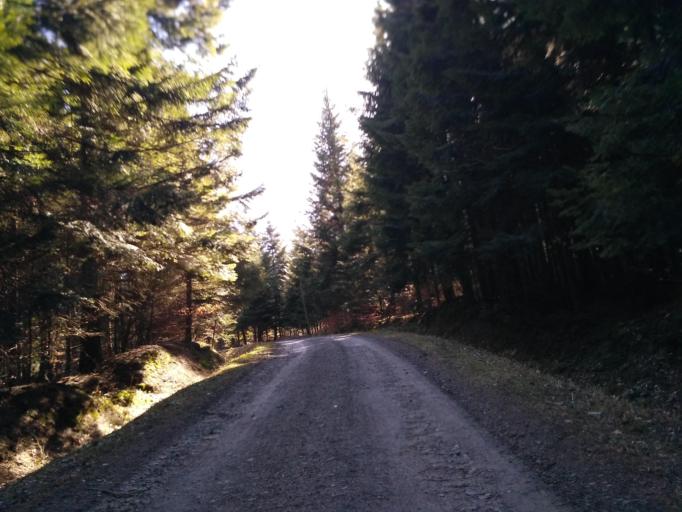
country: PL
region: Subcarpathian Voivodeship
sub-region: Powiat strzyzowski
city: Babica
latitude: 49.9537
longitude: 21.8677
